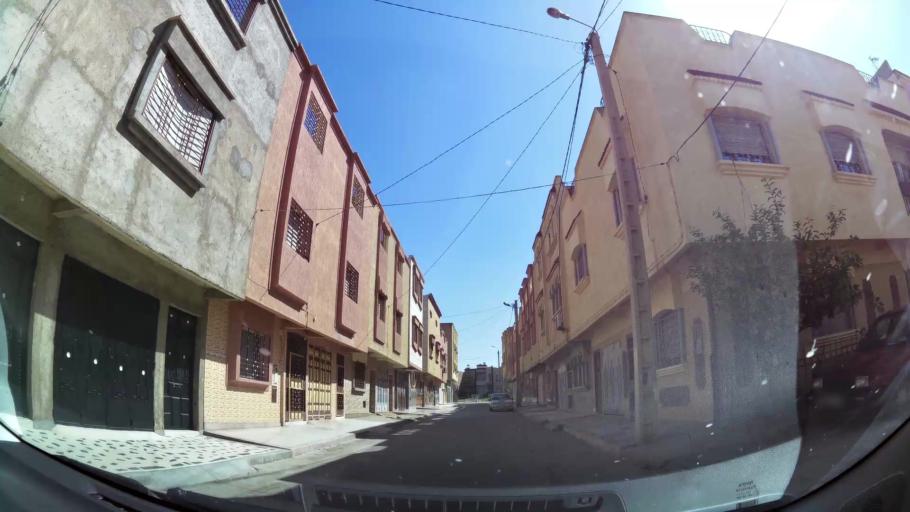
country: MA
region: Oriental
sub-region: Oujda-Angad
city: Oujda
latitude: 34.6790
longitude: -1.9354
